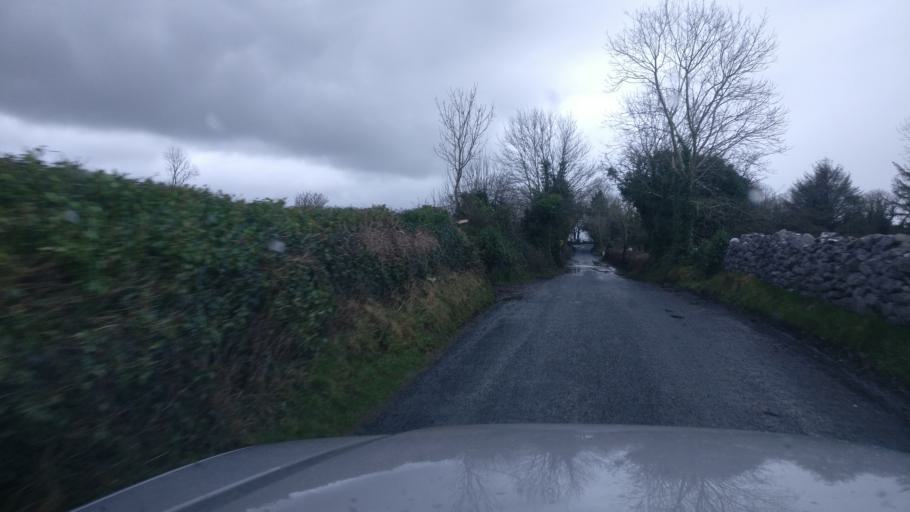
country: IE
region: Connaught
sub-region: County Galway
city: Loughrea
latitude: 53.2016
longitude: -8.6618
